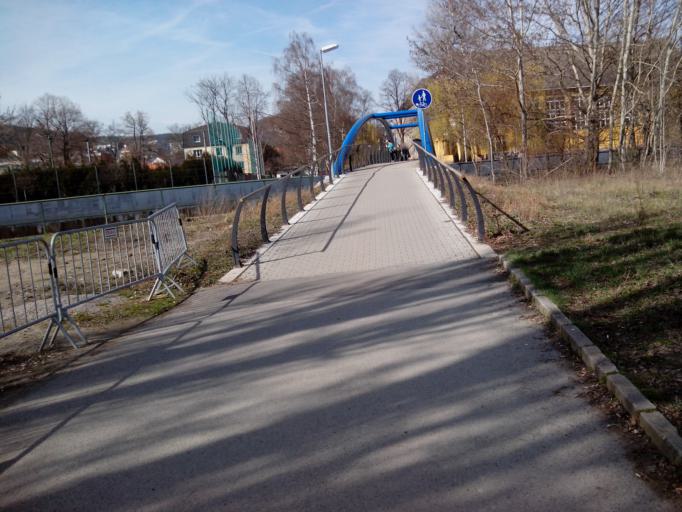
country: CZ
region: Central Bohemia
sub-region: Okres Beroun
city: Beroun
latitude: 49.9596
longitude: 14.0750
